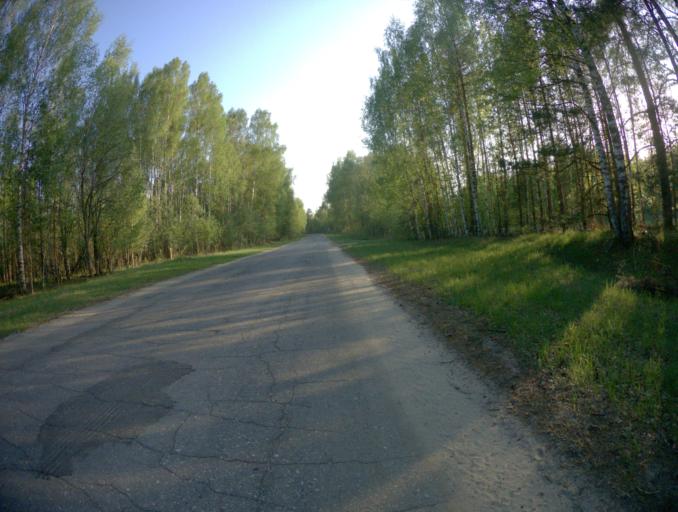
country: RU
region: Vladimir
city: Vyazniki
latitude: 56.3320
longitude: 42.1260
